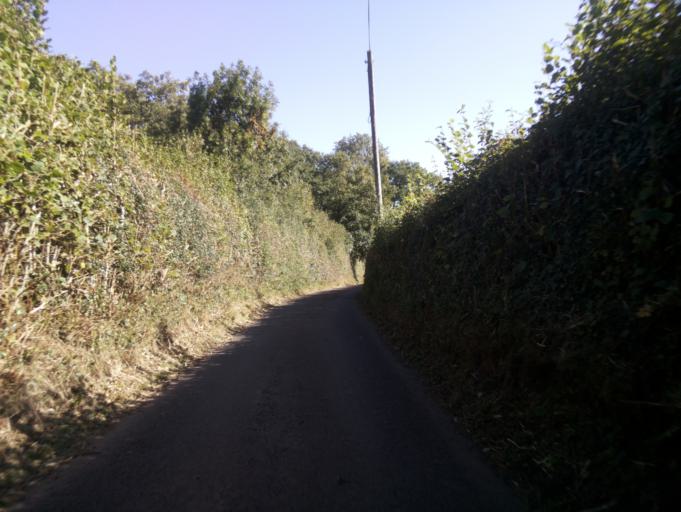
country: GB
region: Wales
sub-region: Torfaen County Borough
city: Cwmbran
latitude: 51.6239
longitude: -3.0429
